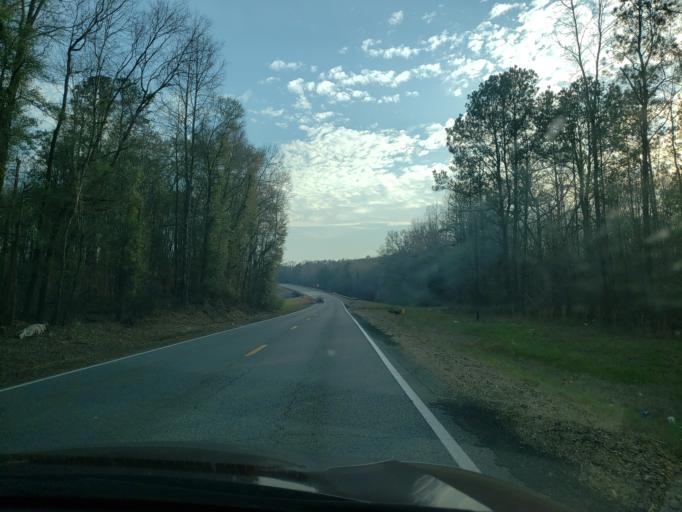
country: US
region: Alabama
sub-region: Hale County
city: Moundville
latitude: 32.9333
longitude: -87.6329
